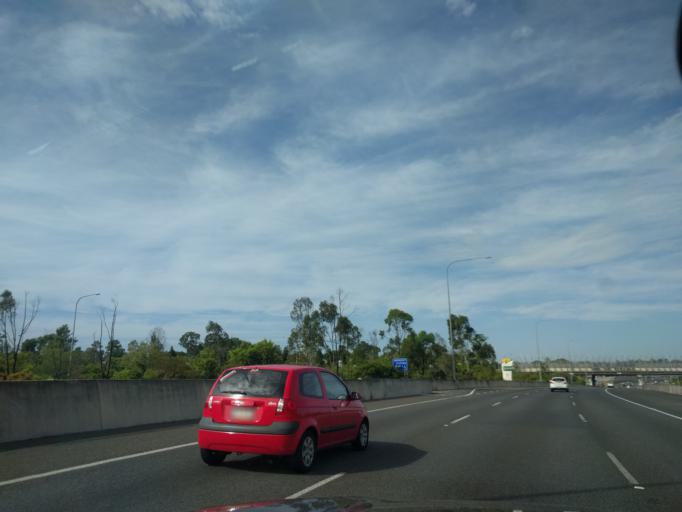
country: AU
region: Queensland
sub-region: Brisbane
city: Wacol
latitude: -27.6051
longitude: 152.9172
